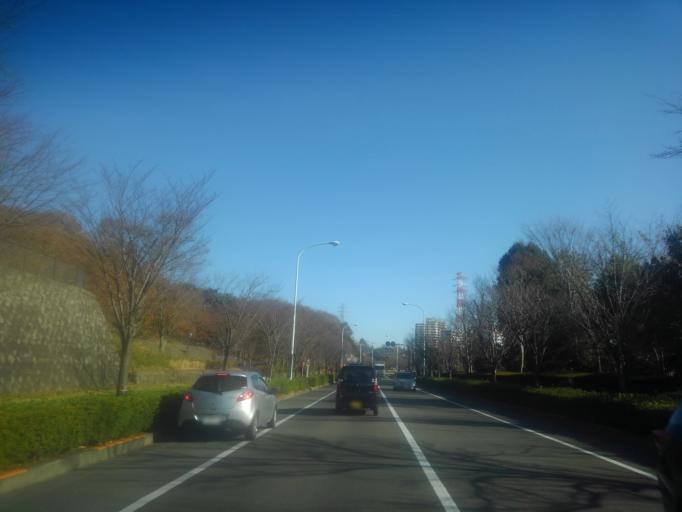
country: JP
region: Tokyo
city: Kokubunji
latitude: 35.6274
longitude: 139.4738
